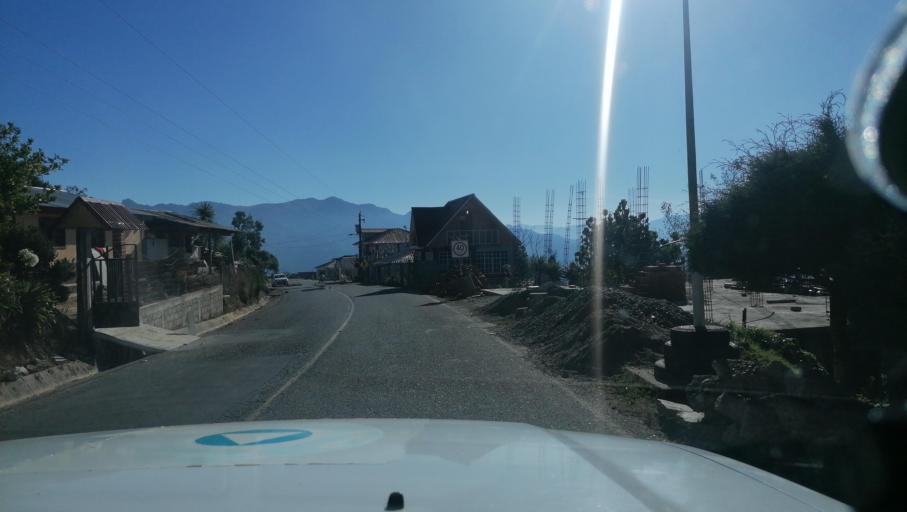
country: MX
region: Chiapas
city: Motozintla de Mendoza
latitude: 15.2379
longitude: -92.2327
